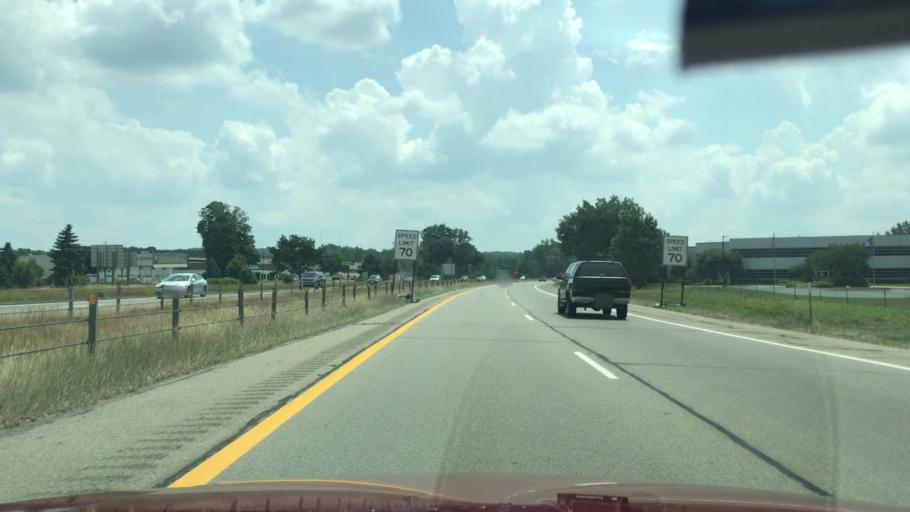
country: US
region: Michigan
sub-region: Kent County
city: Cutlerville
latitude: 42.8230
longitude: -85.6704
